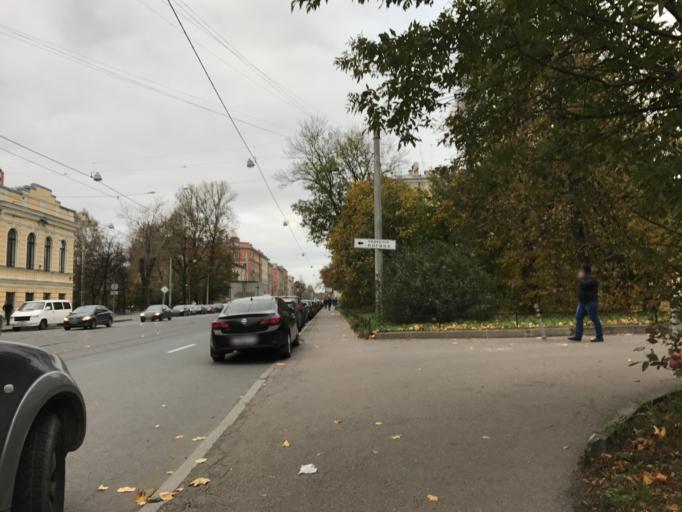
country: RU
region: St.-Petersburg
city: Obukhovo
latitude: 59.8997
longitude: 30.4290
